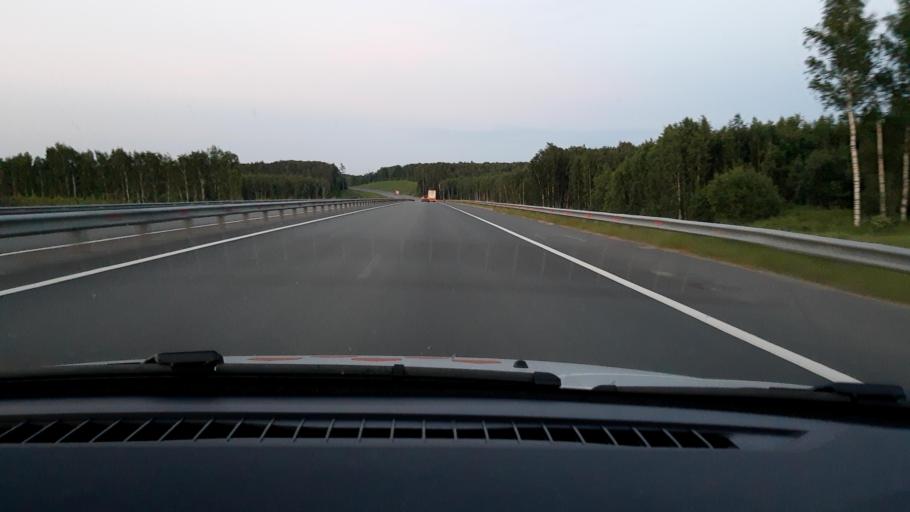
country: RU
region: Nizjnij Novgorod
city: Afonino
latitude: 56.1032
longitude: 44.0112
